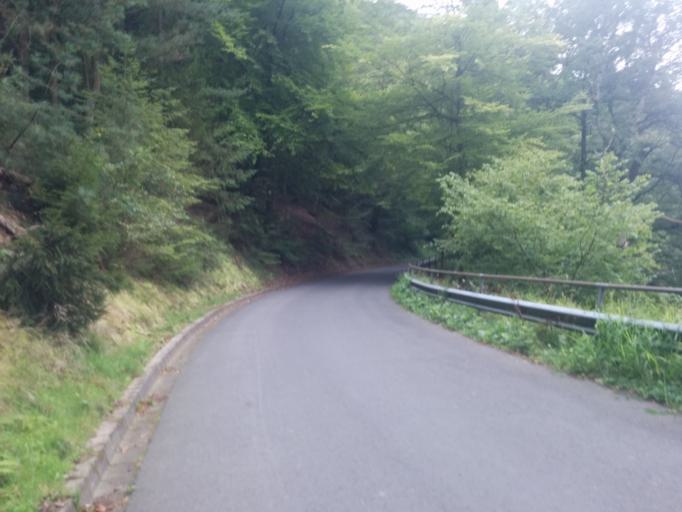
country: DE
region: Rheinland-Pfalz
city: Bernkastel-Kues
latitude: 49.9068
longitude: 7.0811
